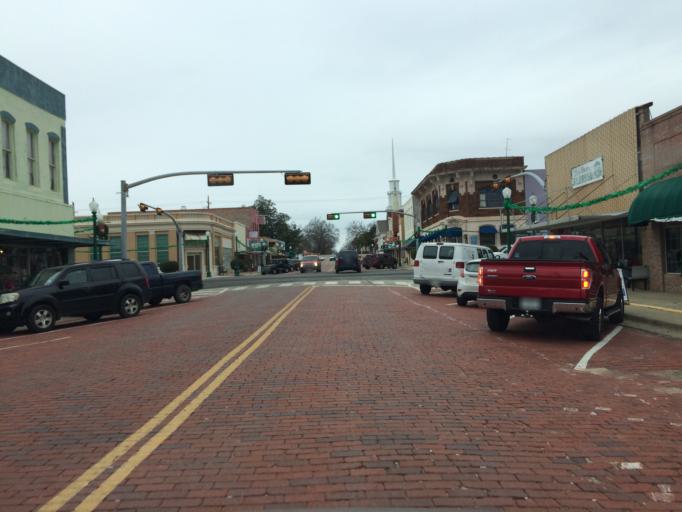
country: US
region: Texas
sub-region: Wood County
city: Mineola
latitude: 32.6631
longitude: -95.4894
